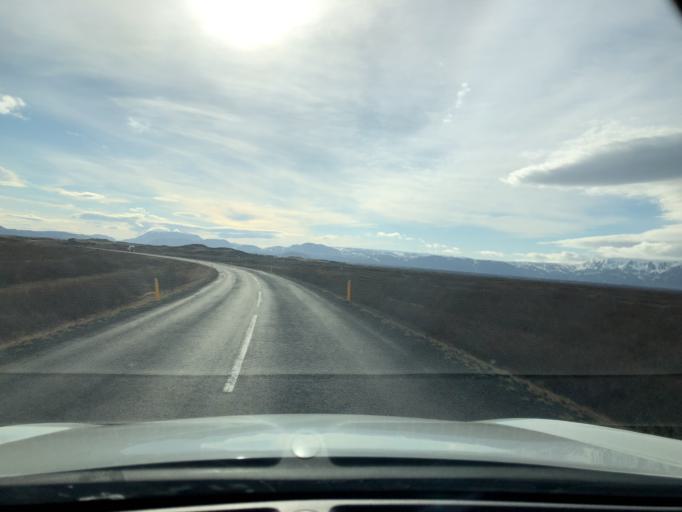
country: IS
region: Northeast
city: Laugar
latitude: 65.5711
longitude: -17.0808
